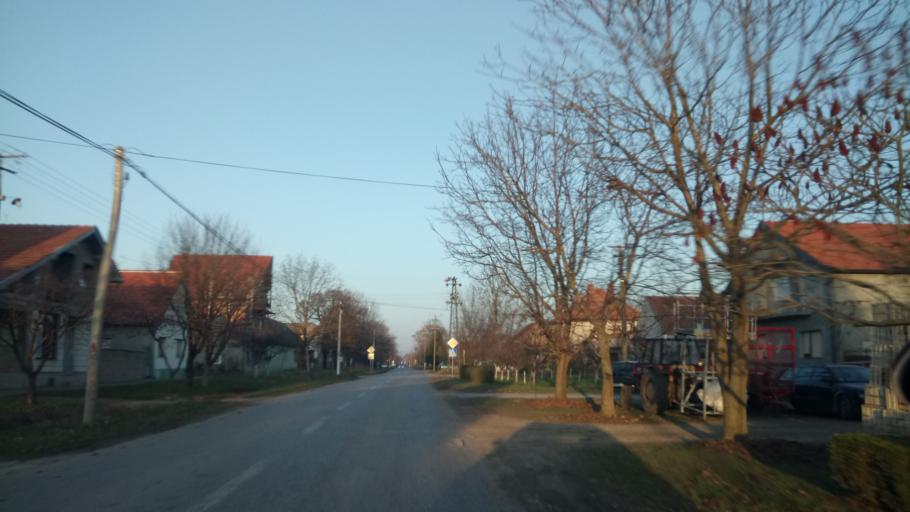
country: RS
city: Novi Slankamen
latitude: 45.1173
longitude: 20.2279
